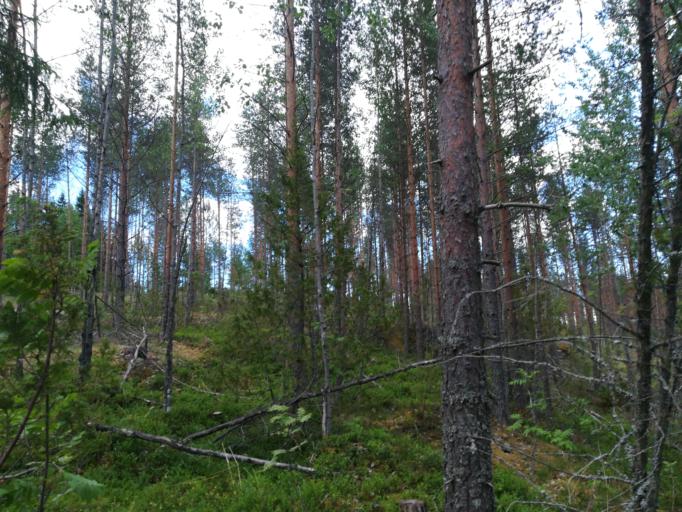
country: FI
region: Southern Savonia
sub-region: Mikkeli
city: Hirvensalmi
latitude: 61.7068
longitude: 26.9713
